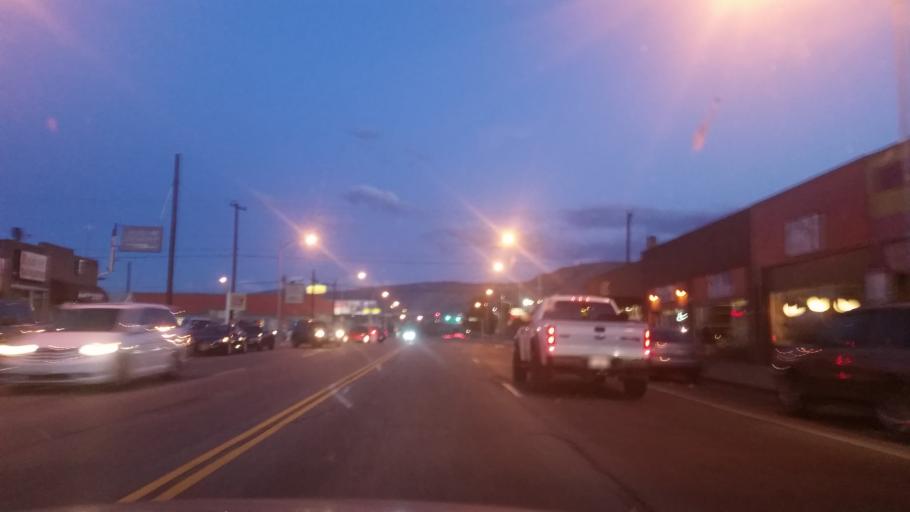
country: US
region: Washington
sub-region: Douglas County
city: East Wenatchee
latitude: 47.4136
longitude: -120.3025
